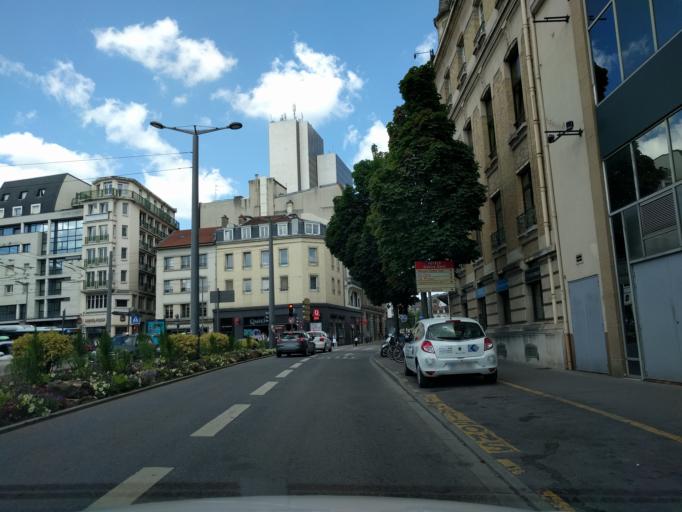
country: FR
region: Lorraine
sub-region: Departement de Meurthe-et-Moselle
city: Nancy
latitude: 48.6890
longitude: 6.1768
